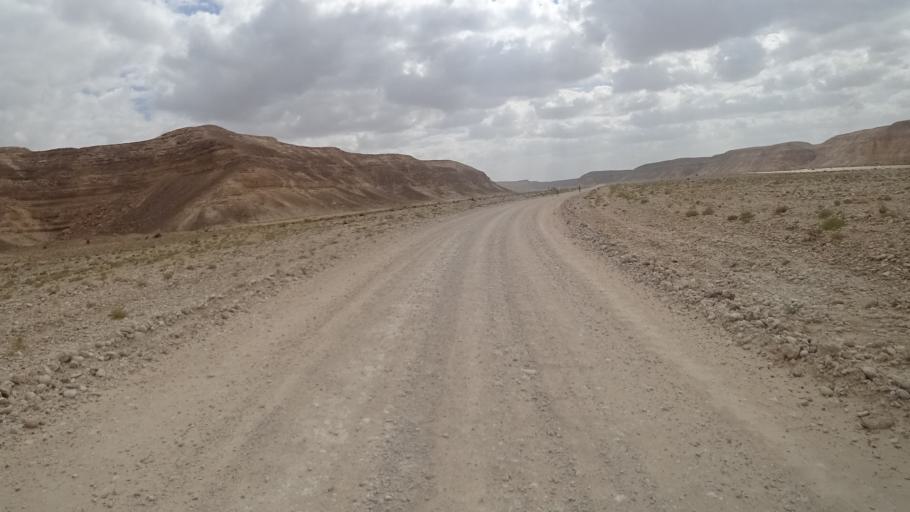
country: YE
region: Al Mahrah
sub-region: Shahan
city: Shihan as Sufla
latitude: 17.4601
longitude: 53.0083
